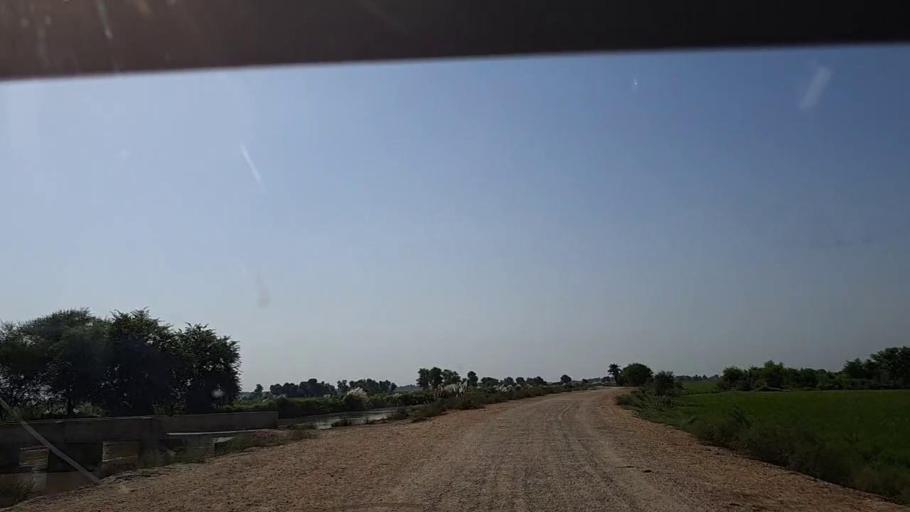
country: PK
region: Sindh
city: Ghauspur
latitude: 28.1840
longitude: 69.0726
